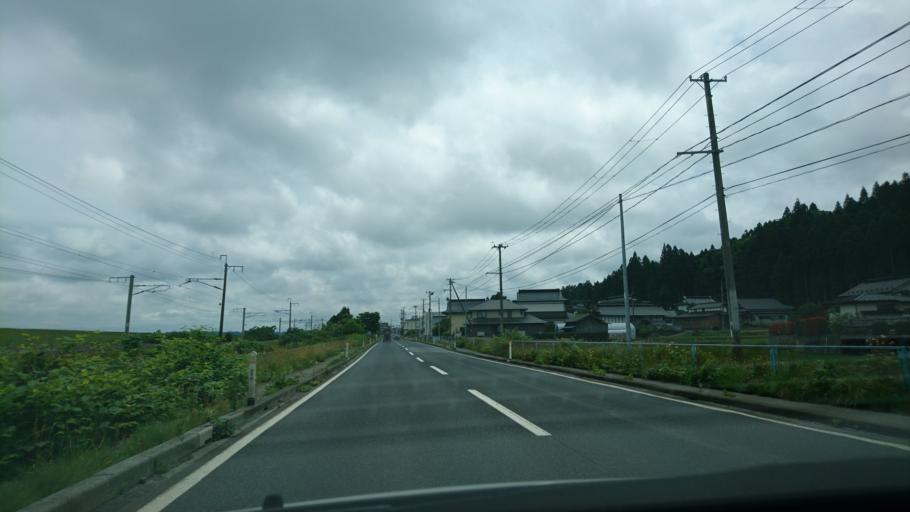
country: JP
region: Iwate
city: Ichinoseki
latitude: 38.9603
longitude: 141.1283
